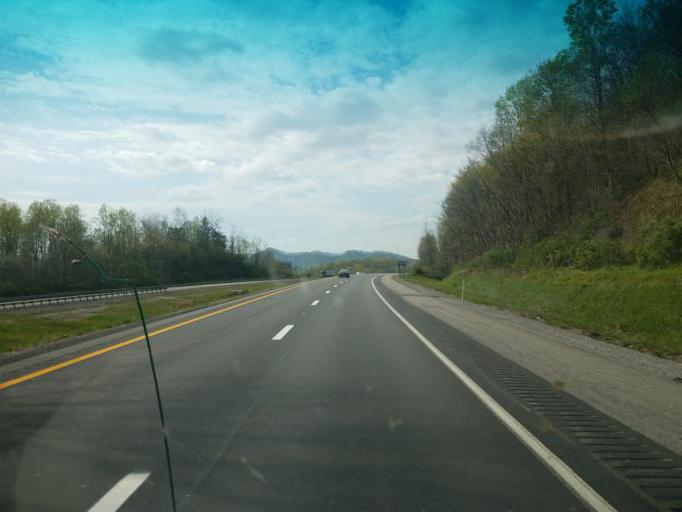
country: US
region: West Virginia
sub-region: Raleigh County
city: Bradley
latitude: 37.9107
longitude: -81.2678
